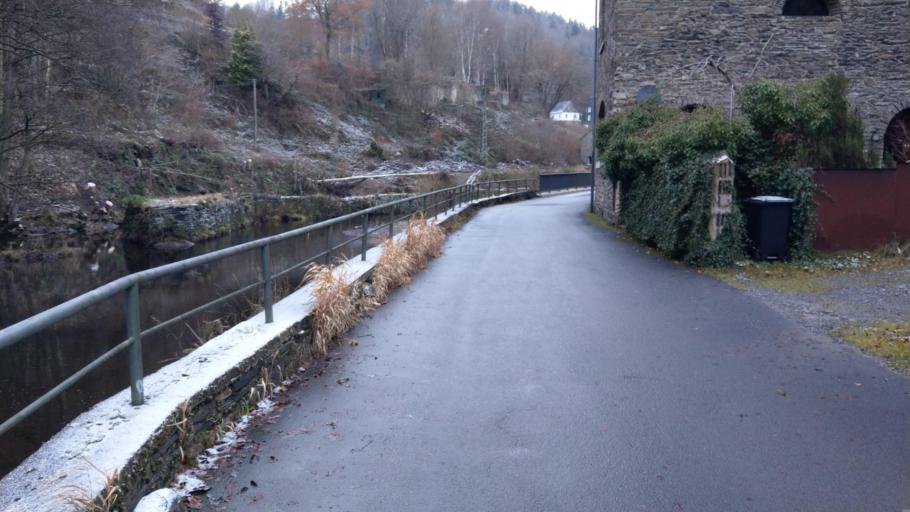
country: DE
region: North Rhine-Westphalia
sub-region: Regierungsbezirk Koln
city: Monschau
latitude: 50.5524
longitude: 6.2463
